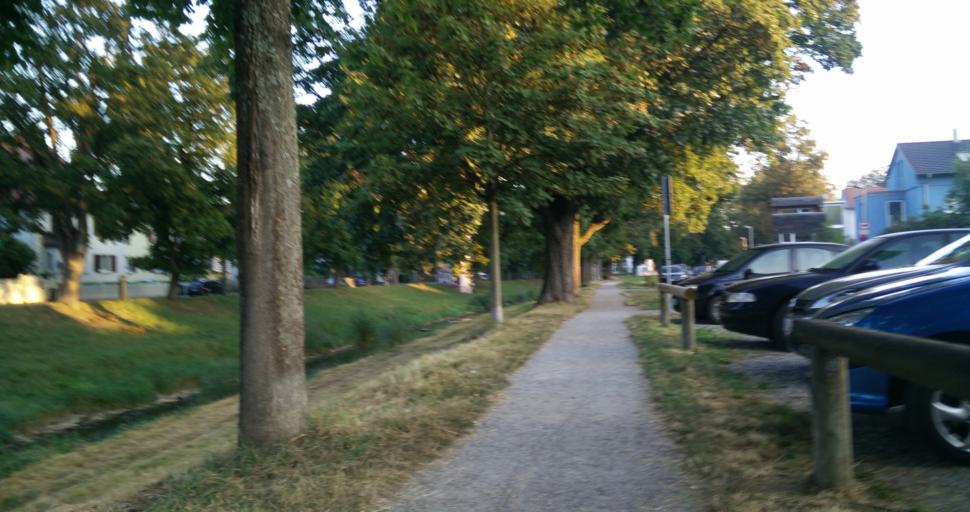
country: DE
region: Baden-Wuerttemberg
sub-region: Tuebingen Region
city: Tuebingen
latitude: 48.5084
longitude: 9.0562
